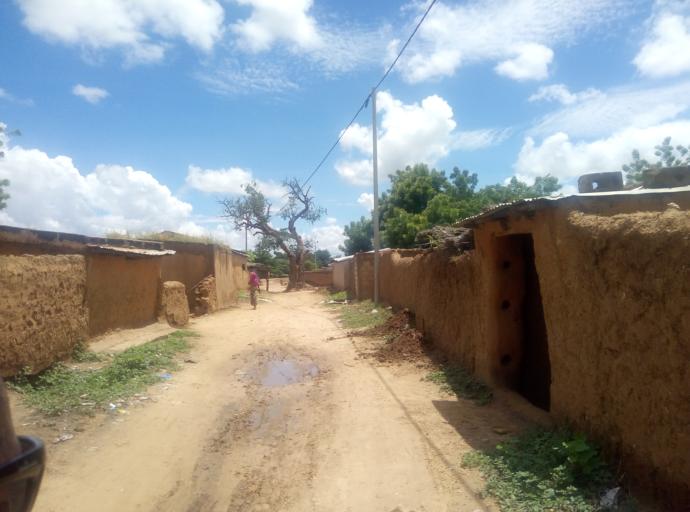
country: ML
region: Kayes
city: Yelimane
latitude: 15.1258
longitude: -10.7281
